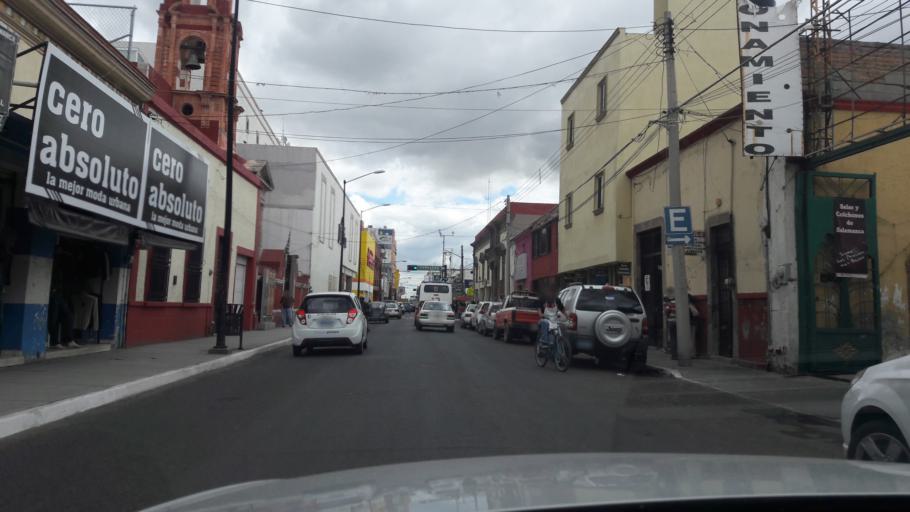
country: MX
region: Guanajuato
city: Salamanca
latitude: 20.5701
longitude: -101.1985
